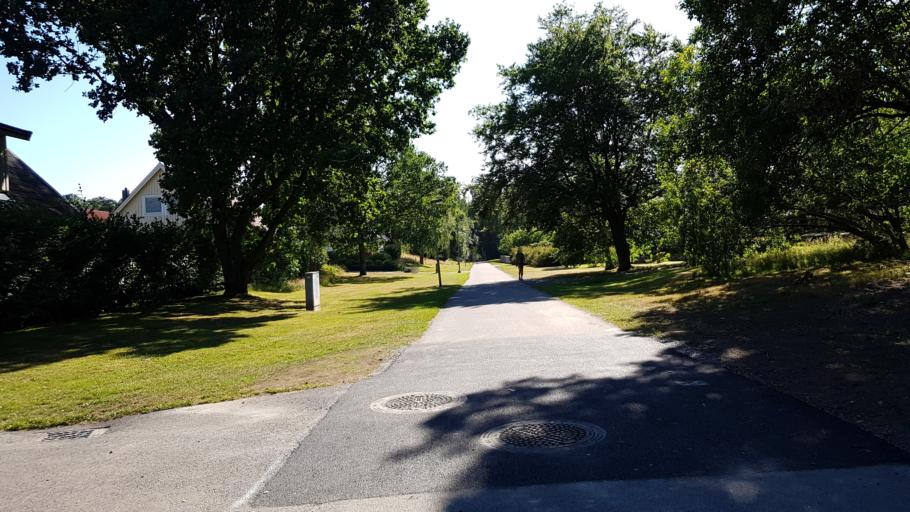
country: SE
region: Vaestra Goetaland
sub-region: Harryda Kommun
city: Molnlycke
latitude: 57.6501
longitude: 12.1175
